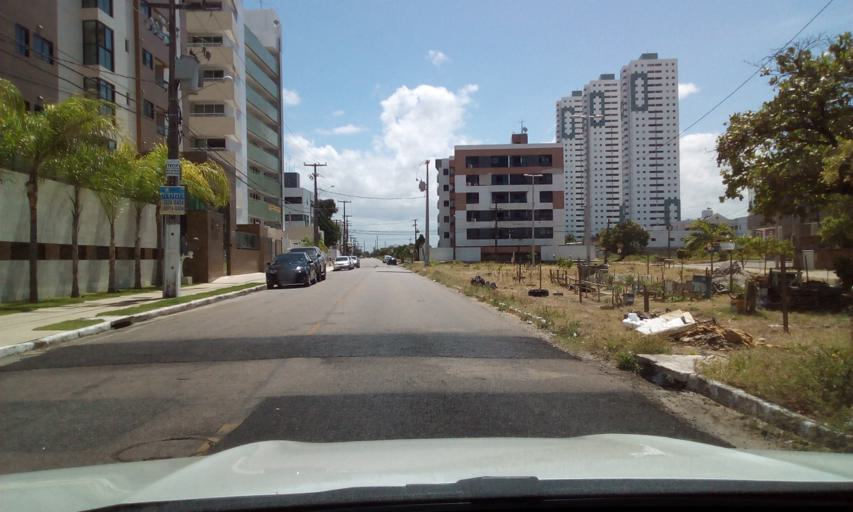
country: BR
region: Paraiba
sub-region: Joao Pessoa
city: Joao Pessoa
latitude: -7.0728
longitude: -34.8375
